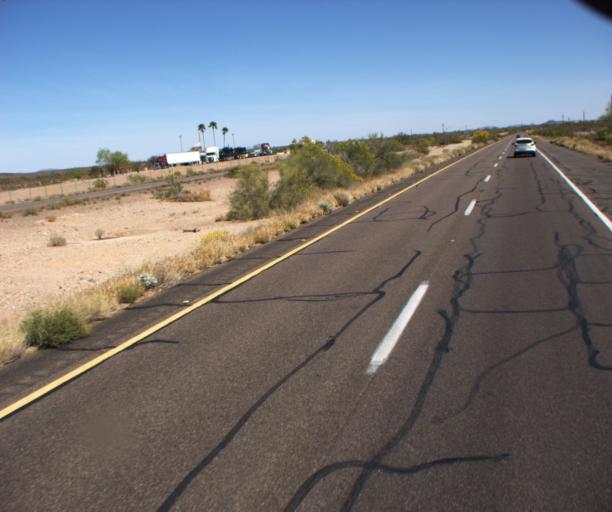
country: US
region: Arizona
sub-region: Maricopa County
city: Gila Bend
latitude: 32.8534
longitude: -113.2544
